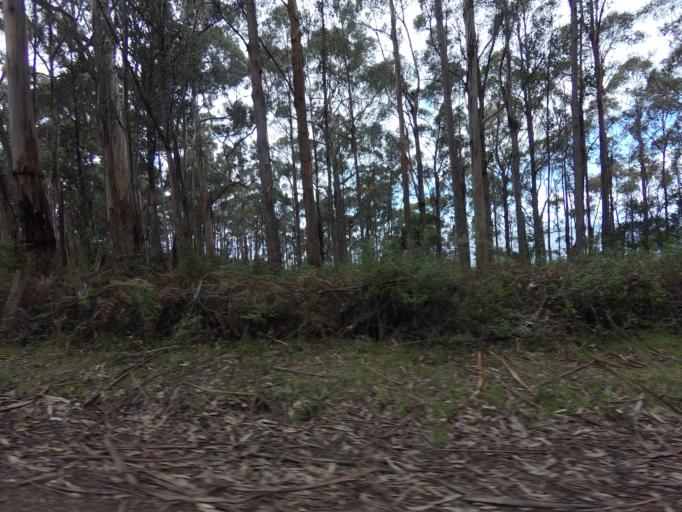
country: AU
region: Tasmania
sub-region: Huon Valley
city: Geeveston
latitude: -43.4171
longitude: 147.0147
